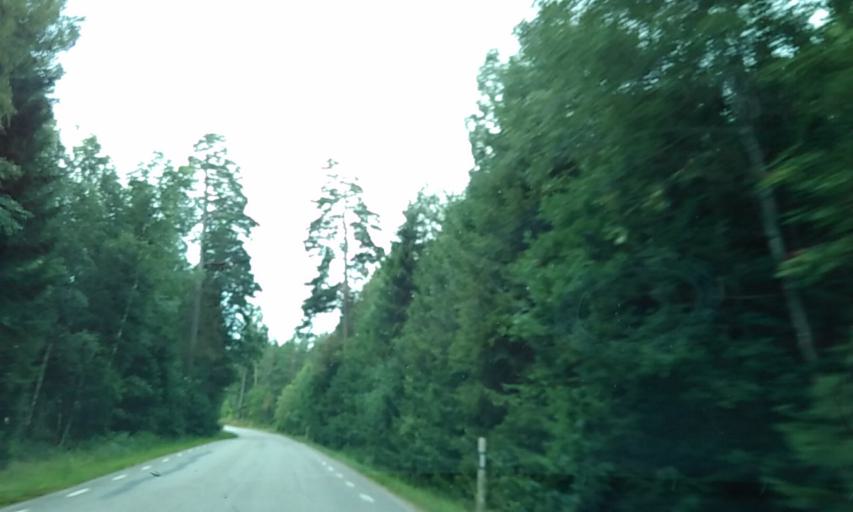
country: SE
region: Vaestra Goetaland
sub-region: Grastorps Kommun
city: Graestorp
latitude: 58.4656
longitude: 12.8070
